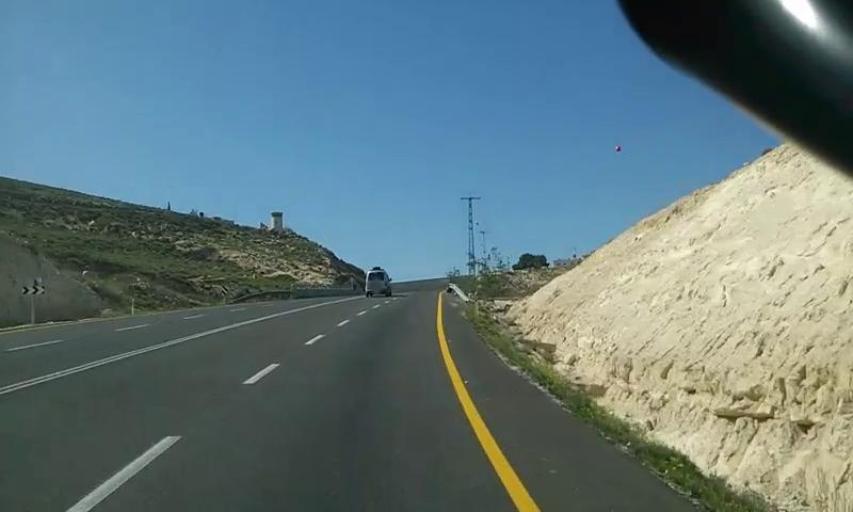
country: PS
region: West Bank
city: Bayt Ta`mar
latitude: 31.6723
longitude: 35.2416
